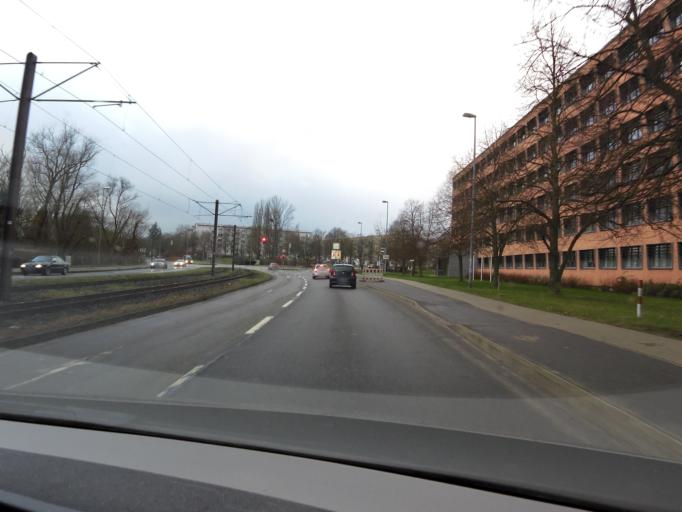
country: DE
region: Mecklenburg-Vorpommern
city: Lankow
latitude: 53.6464
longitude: 11.3793
